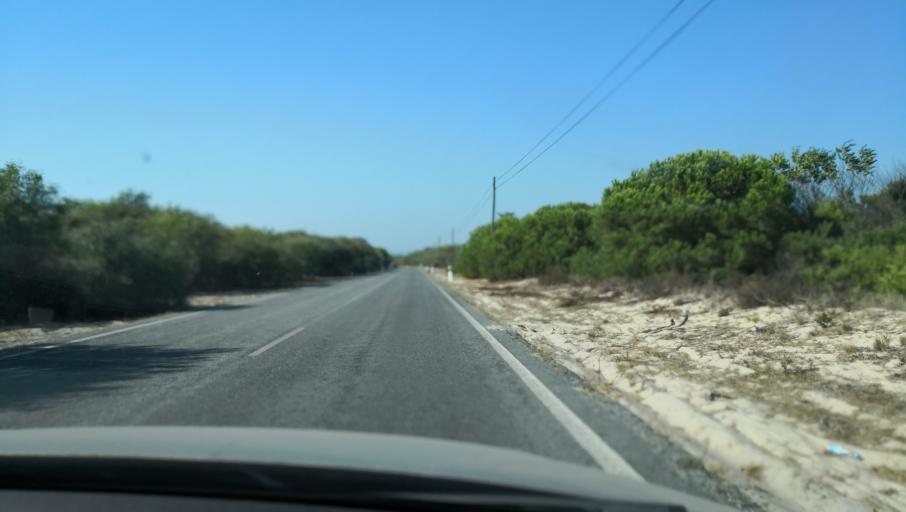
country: PT
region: Setubal
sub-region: Setubal
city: Setubal
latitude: 38.4066
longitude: -8.8100
